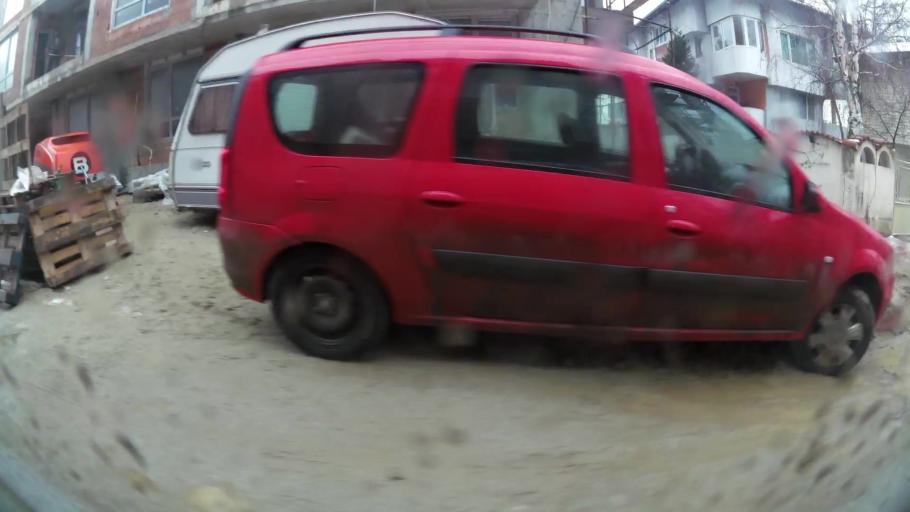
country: BG
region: Sofia-Capital
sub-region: Stolichna Obshtina
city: Sofia
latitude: 42.6798
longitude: 23.2590
